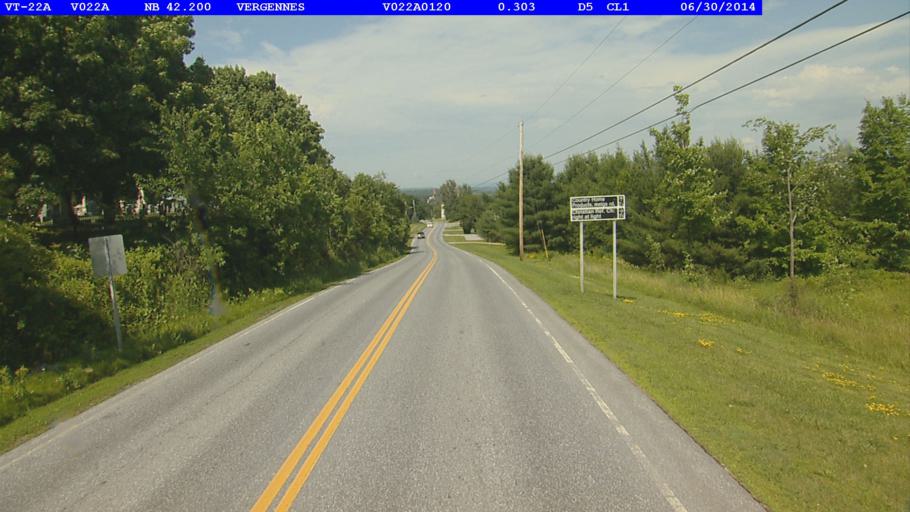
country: US
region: Vermont
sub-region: Addison County
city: Vergennes
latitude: 44.1581
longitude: -73.2645
